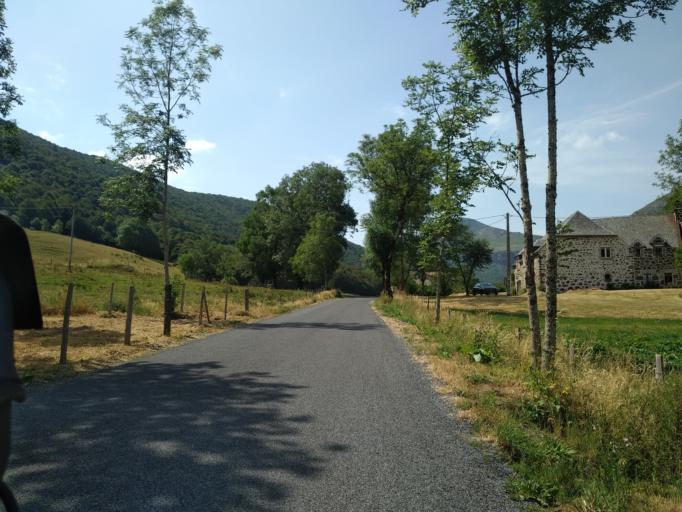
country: FR
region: Auvergne
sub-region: Departement du Cantal
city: Riom-es-Montagnes
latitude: 45.1362
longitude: 2.6977
